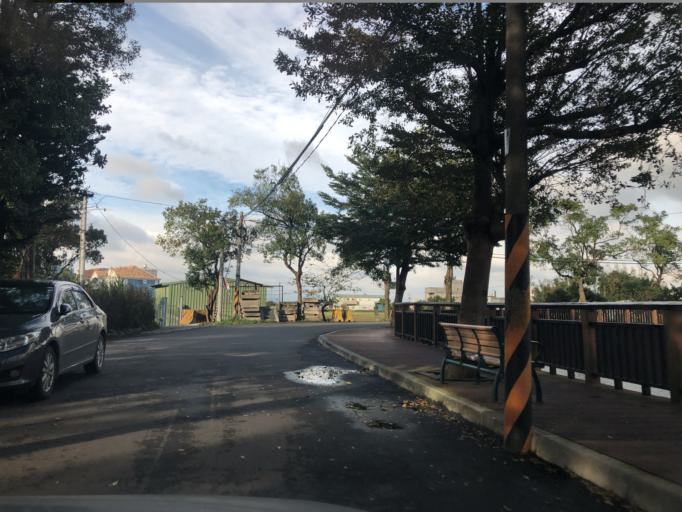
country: TW
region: Taiwan
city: Daxi
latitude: 24.9052
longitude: 121.2659
